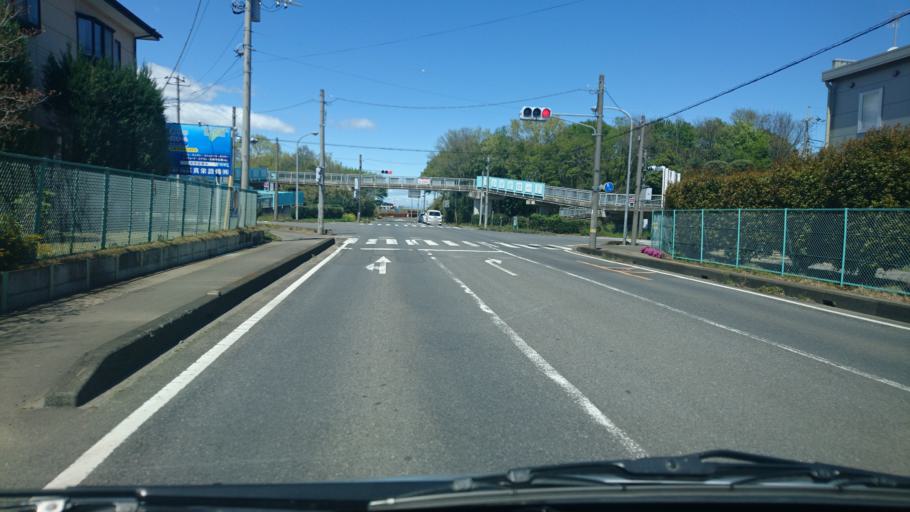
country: JP
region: Ibaraki
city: Shimodate
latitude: 36.2701
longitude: 139.9490
